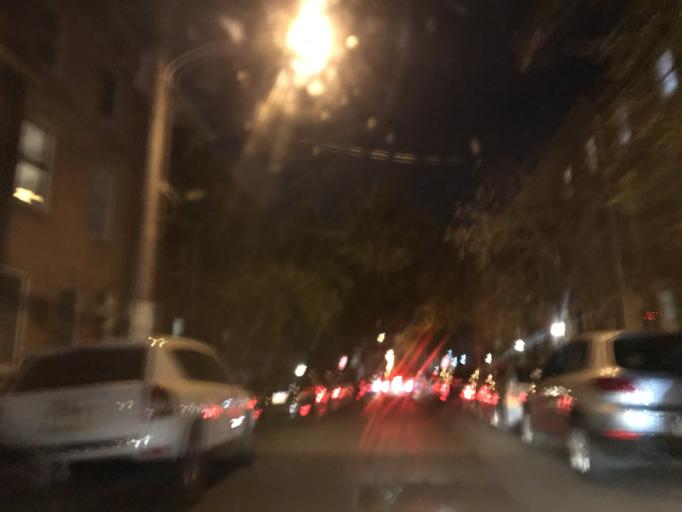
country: US
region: Pennsylvania
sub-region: Philadelphia County
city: Philadelphia
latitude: 39.9426
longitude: -75.1587
